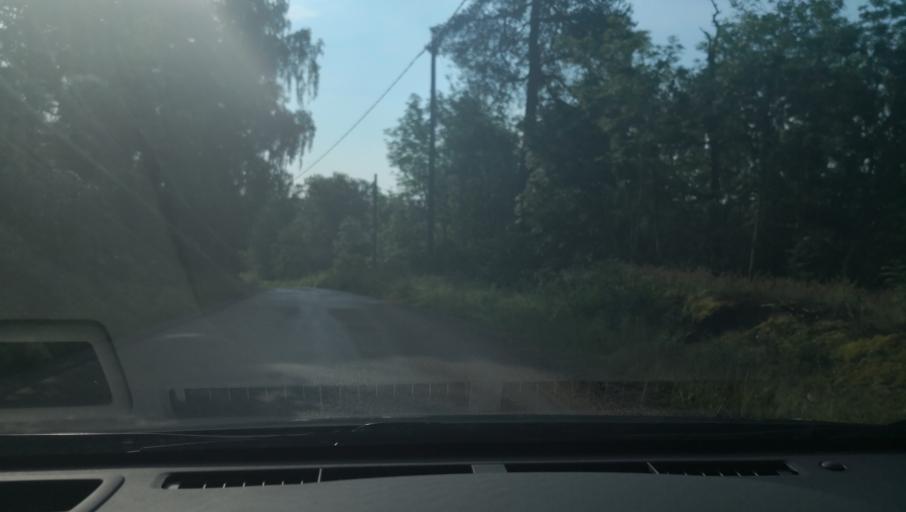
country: SE
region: Vaestmanland
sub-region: Arboga Kommun
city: Tyringe
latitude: 59.3938
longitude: 15.9351
